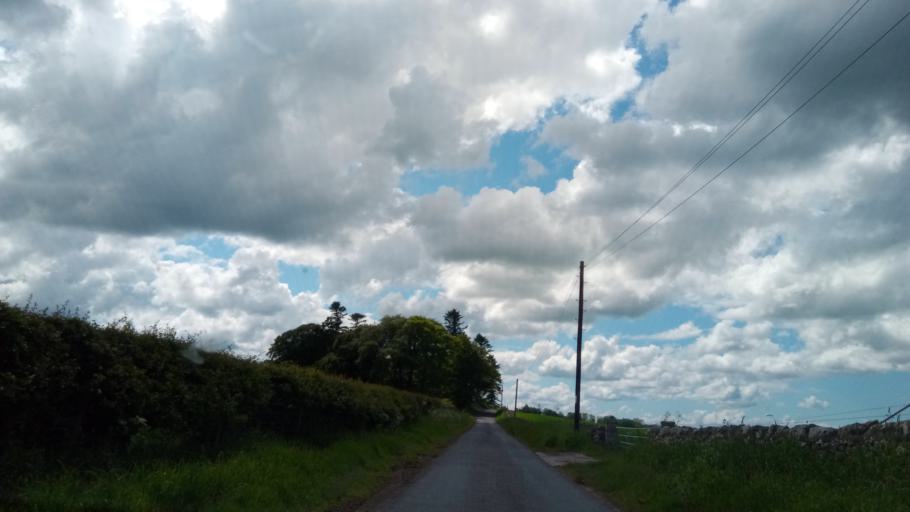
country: GB
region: Scotland
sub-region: The Scottish Borders
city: Coldstream
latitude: 55.5872
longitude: -2.2998
